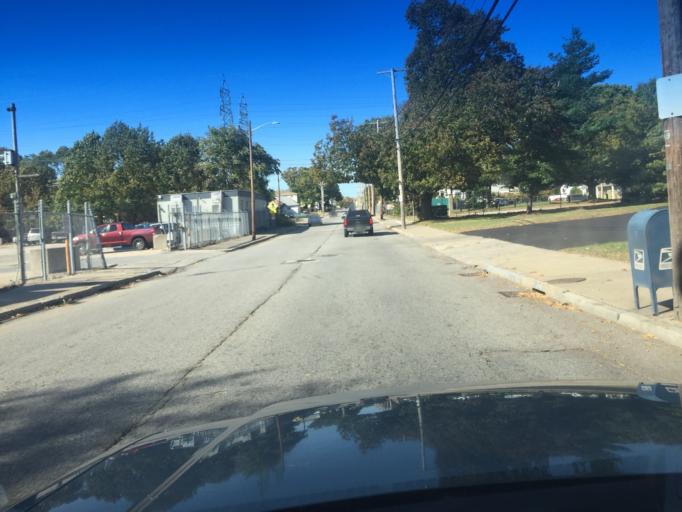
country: US
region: Rhode Island
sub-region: Providence County
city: Pawtucket
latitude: 41.8630
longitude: -71.3707
